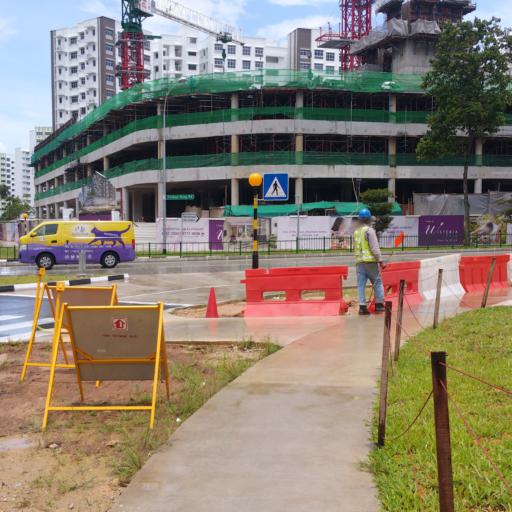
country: MY
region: Johor
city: Kampung Pasir Gudang Baru
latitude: 1.4176
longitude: 103.8405
